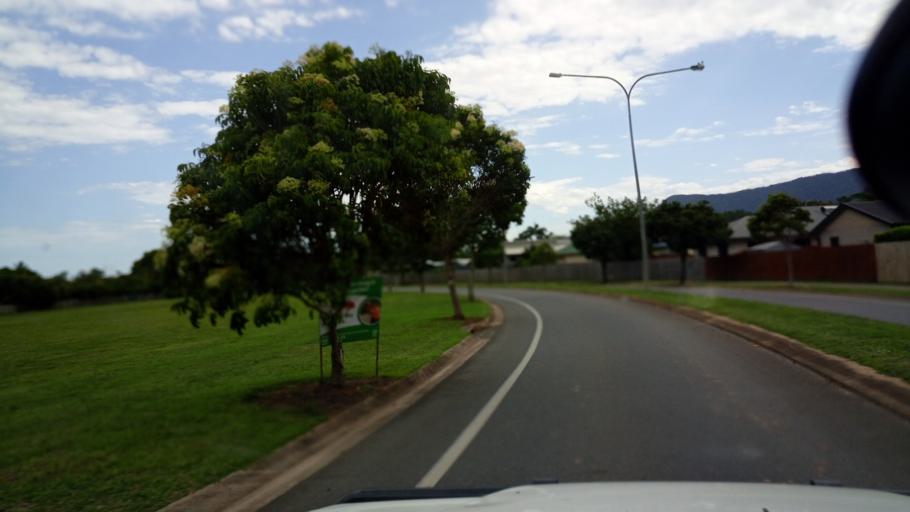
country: AU
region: Queensland
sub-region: Cairns
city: Woree
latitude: -16.9249
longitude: 145.7294
